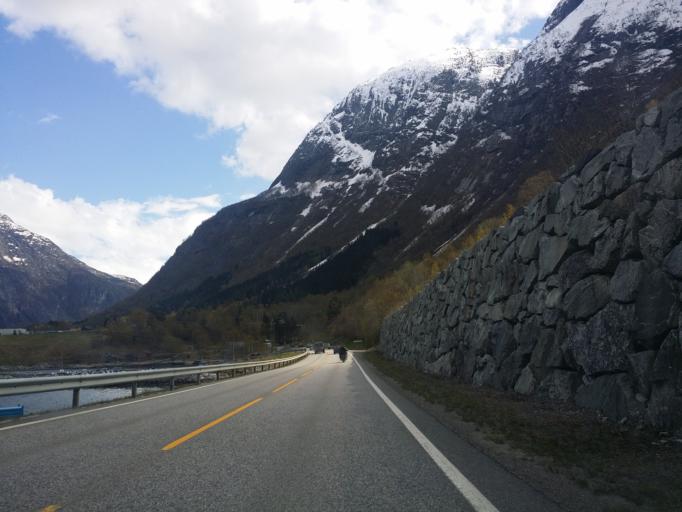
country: NO
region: Hordaland
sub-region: Eidfjord
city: Eidfjord
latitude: 60.4660
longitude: 7.0547
